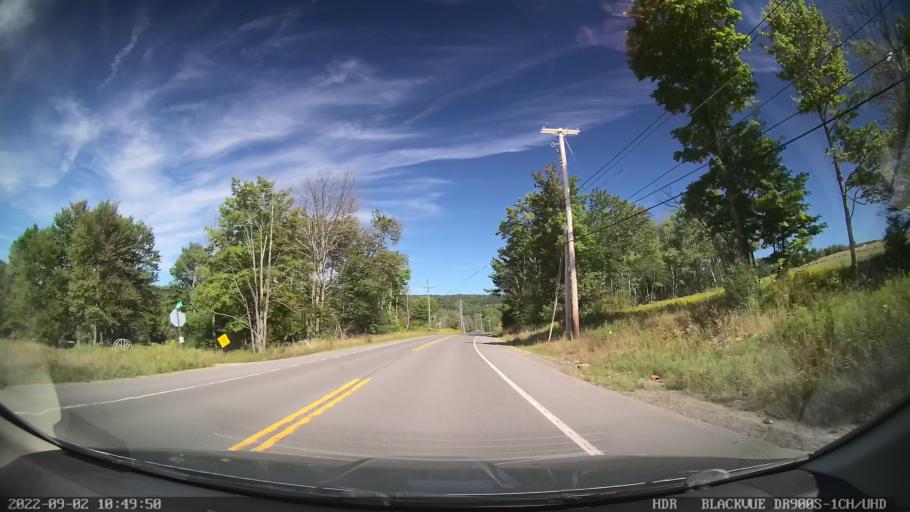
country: US
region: Pennsylvania
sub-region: Tioga County
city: Blossburg
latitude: 41.6054
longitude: -77.1146
